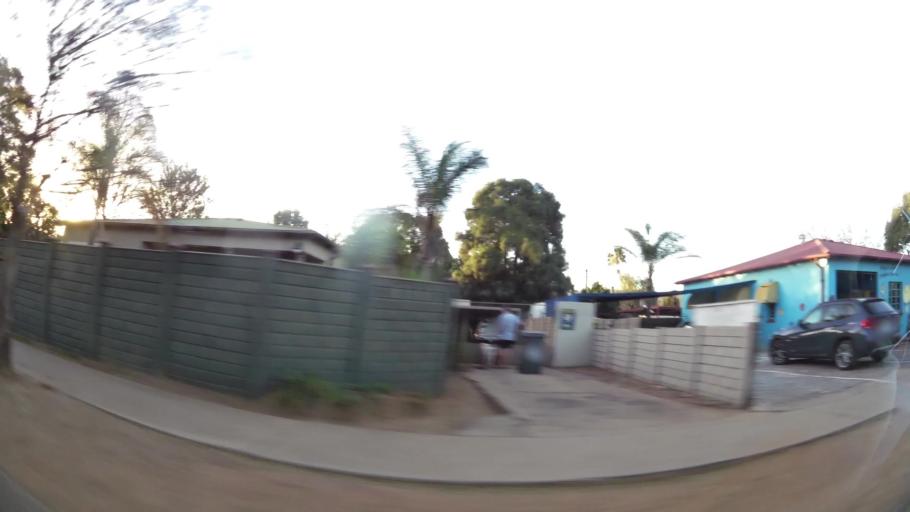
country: ZA
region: Gauteng
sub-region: City of Tshwane Metropolitan Municipality
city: Pretoria
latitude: -25.7126
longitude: 28.2148
